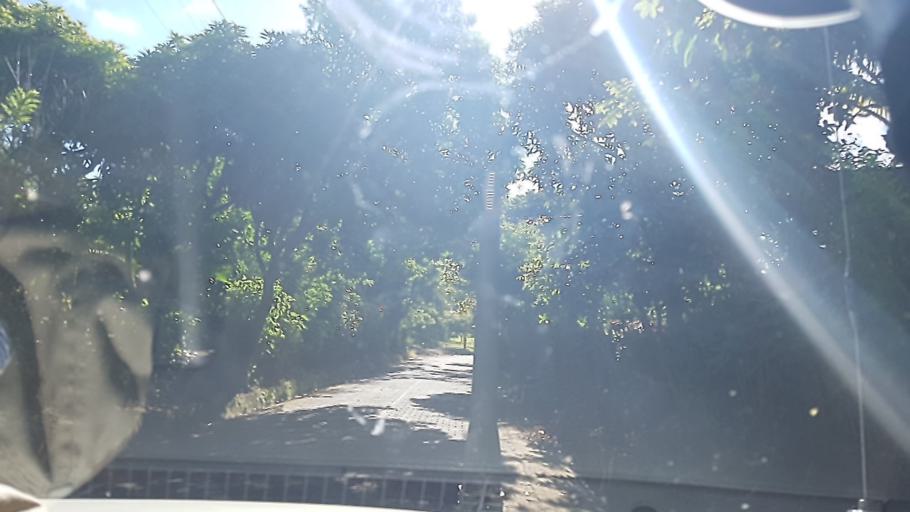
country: NI
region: Carazo
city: La Paz de Oriente
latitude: 11.8320
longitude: -86.1553
